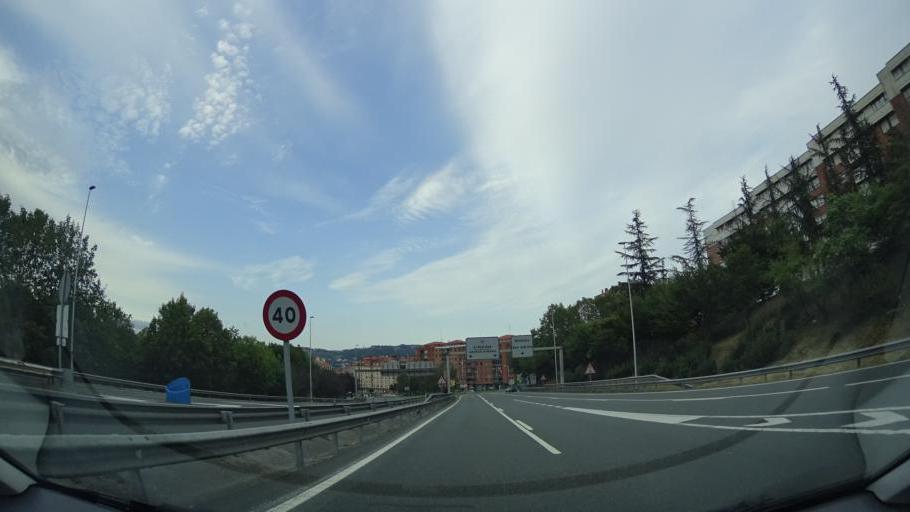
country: ES
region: Basque Country
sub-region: Bizkaia
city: Bilbao
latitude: 43.2490
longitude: -2.9355
